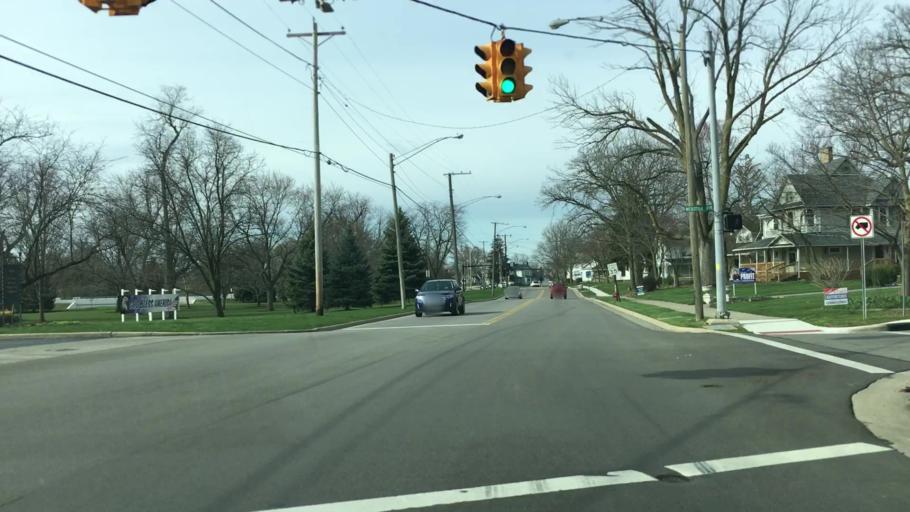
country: US
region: Ohio
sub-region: Van Wert County
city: Van Wert
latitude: 40.8609
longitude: -84.5830
